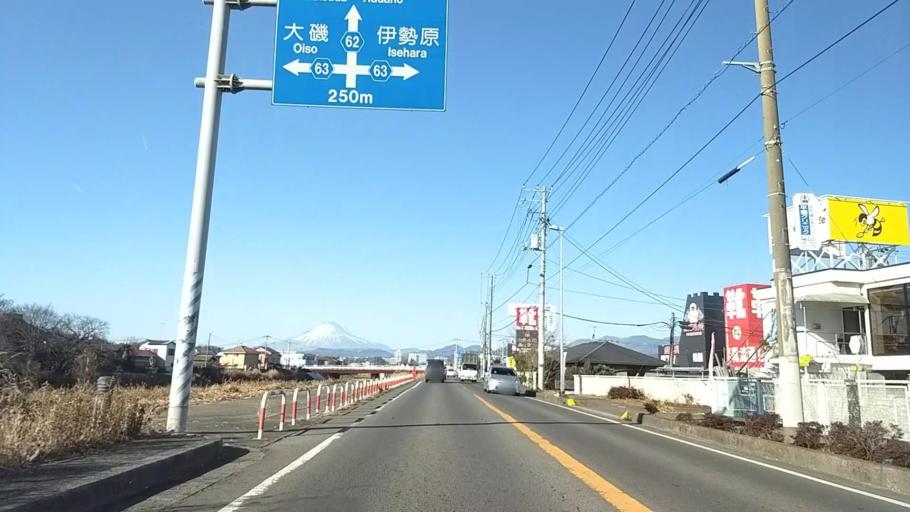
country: JP
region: Kanagawa
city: Isehara
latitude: 35.3589
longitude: 139.3010
